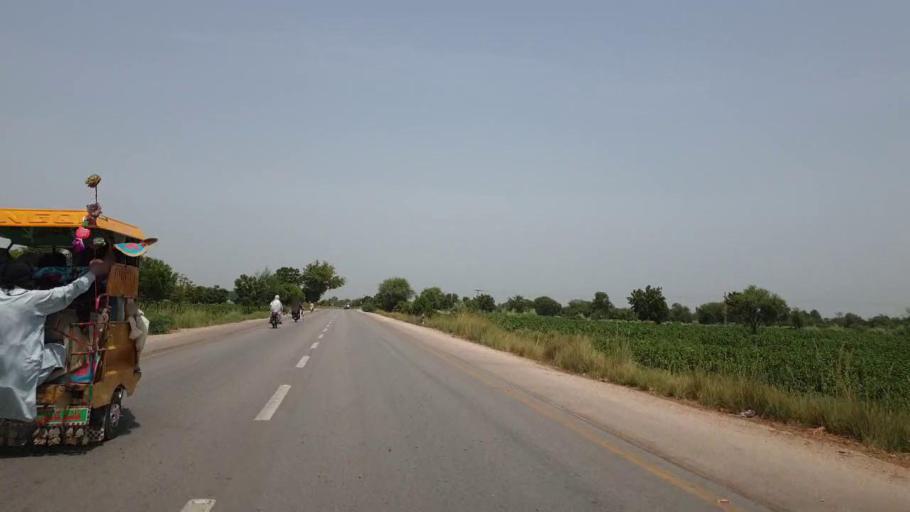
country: PK
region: Sindh
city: Nawabshah
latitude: 26.2430
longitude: 68.4672
